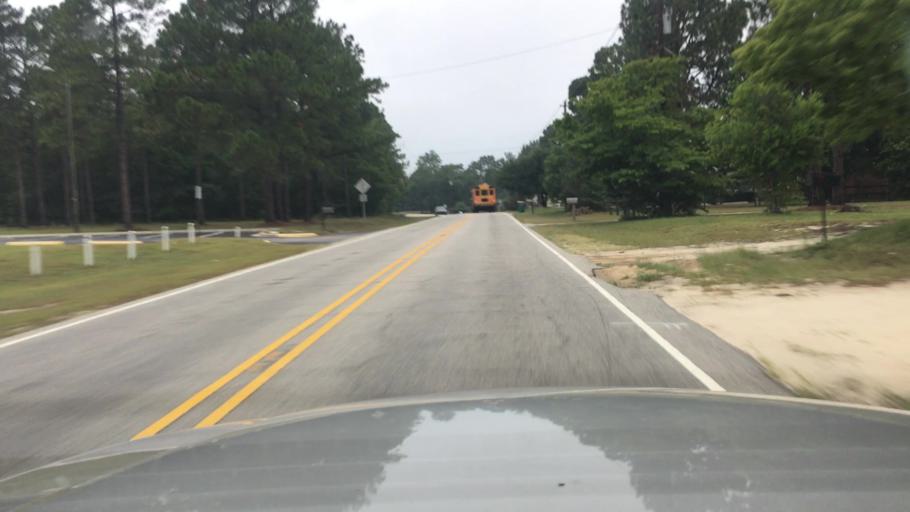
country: US
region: North Carolina
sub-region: Cumberland County
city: Hope Mills
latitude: 34.9738
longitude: -78.9656
